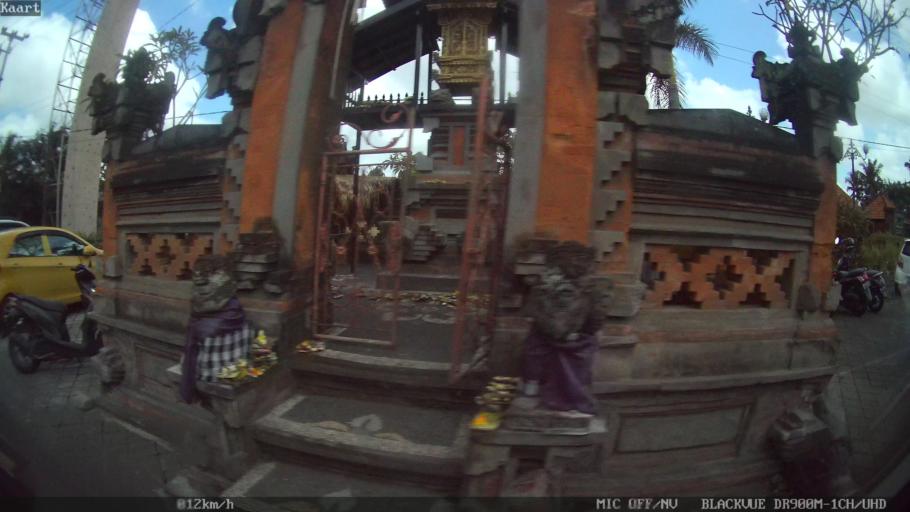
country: ID
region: Bali
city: Banjar Sedang
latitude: -8.5680
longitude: 115.2944
